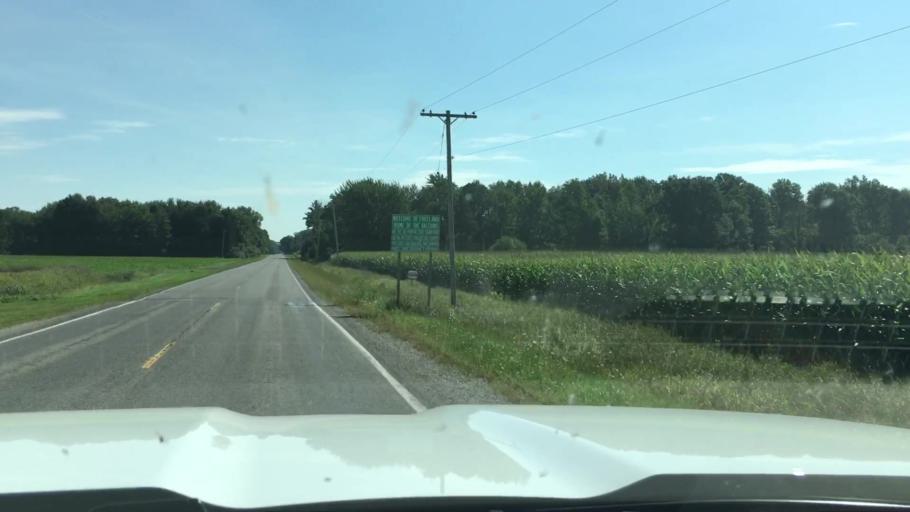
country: US
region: Michigan
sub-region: Saginaw County
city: Freeland
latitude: 43.5253
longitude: -84.1690
